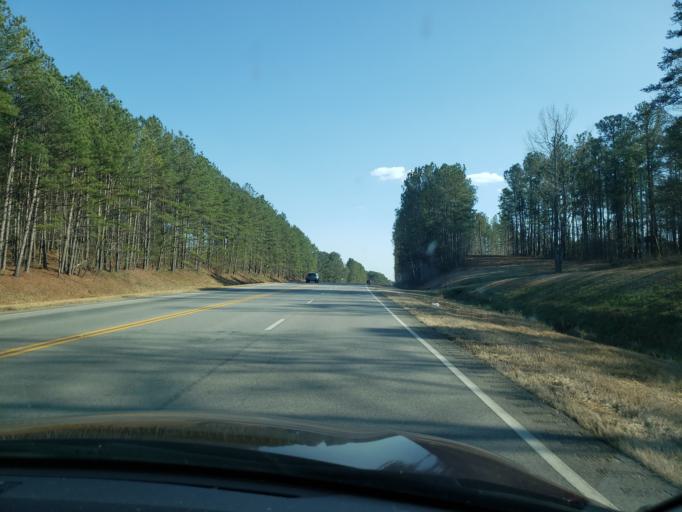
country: US
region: Alabama
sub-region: Randolph County
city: Wedowee
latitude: 33.4650
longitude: -85.5757
